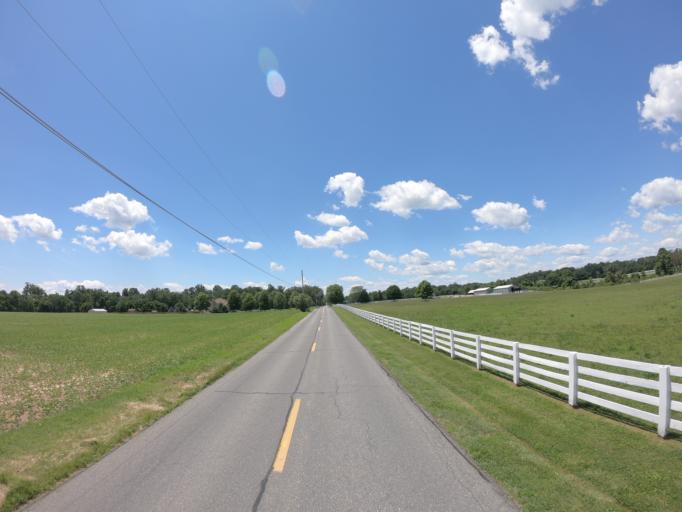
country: US
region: Delaware
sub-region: New Castle County
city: Middletown
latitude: 39.4811
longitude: -75.7535
